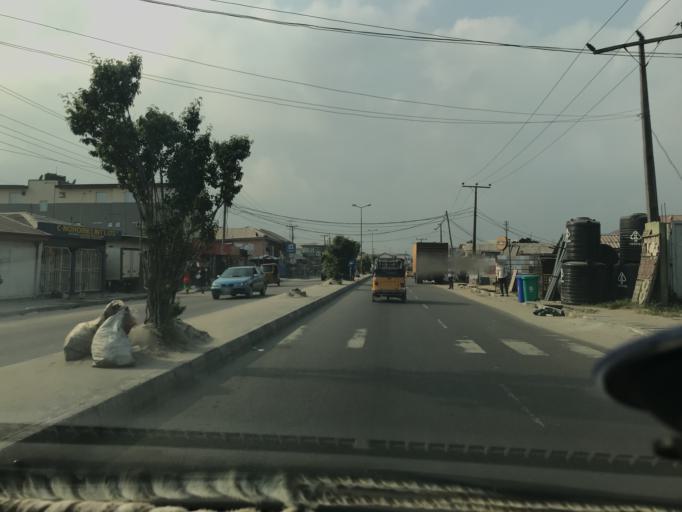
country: NG
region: Lagos
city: Ebute Ikorodu
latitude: 6.4911
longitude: 3.5815
